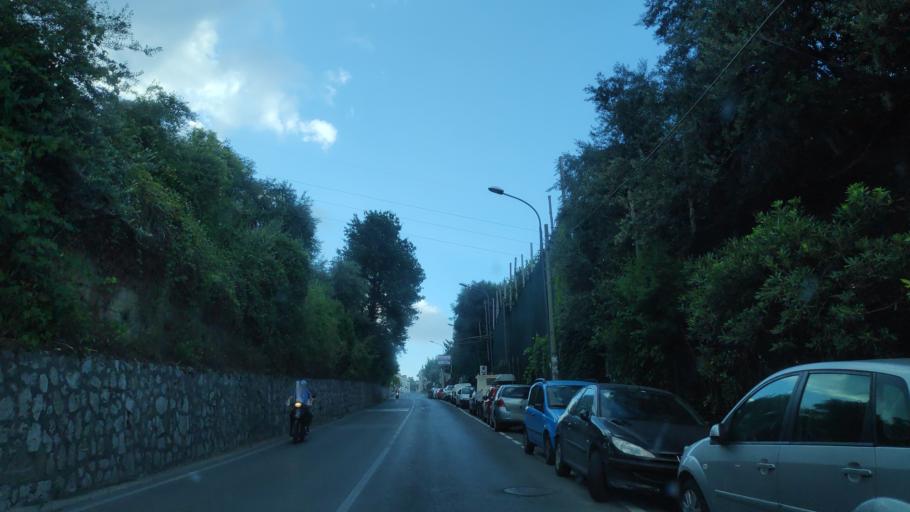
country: IT
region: Campania
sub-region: Provincia di Napoli
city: Piano di Sorrento
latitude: 40.6302
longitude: 14.4206
